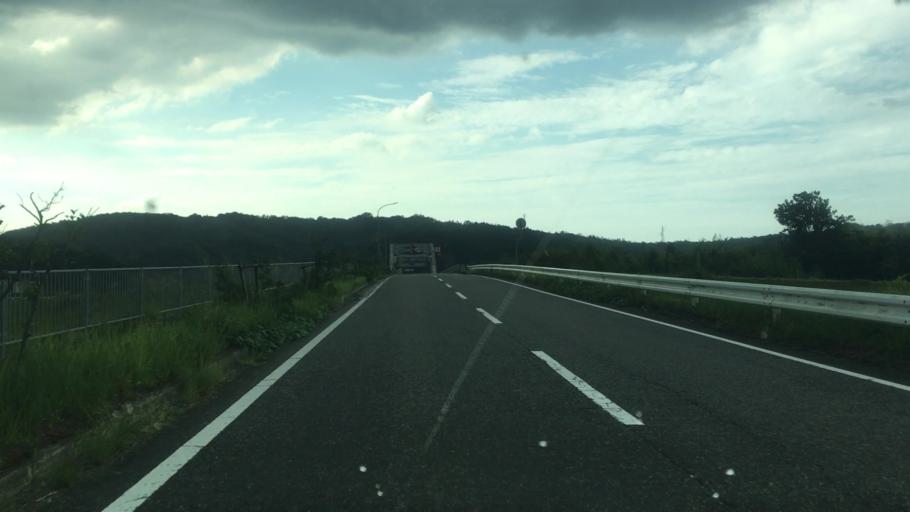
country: JP
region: Hyogo
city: Toyooka
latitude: 35.5040
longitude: 134.8179
